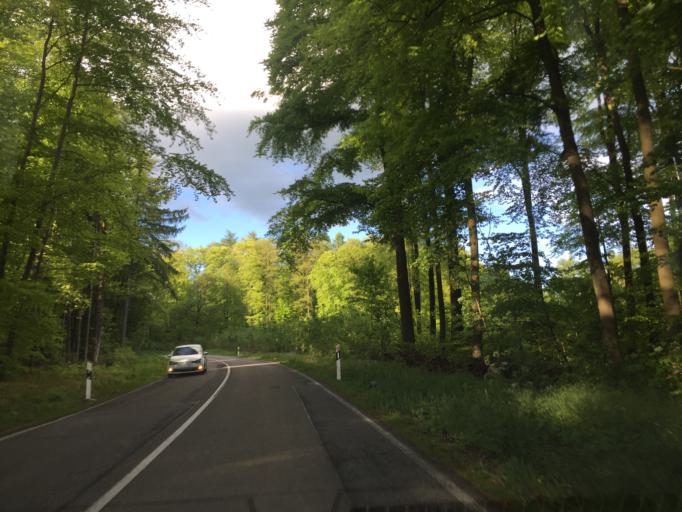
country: DE
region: Rheinland-Pfalz
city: Nauort
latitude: 50.4347
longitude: 7.6357
